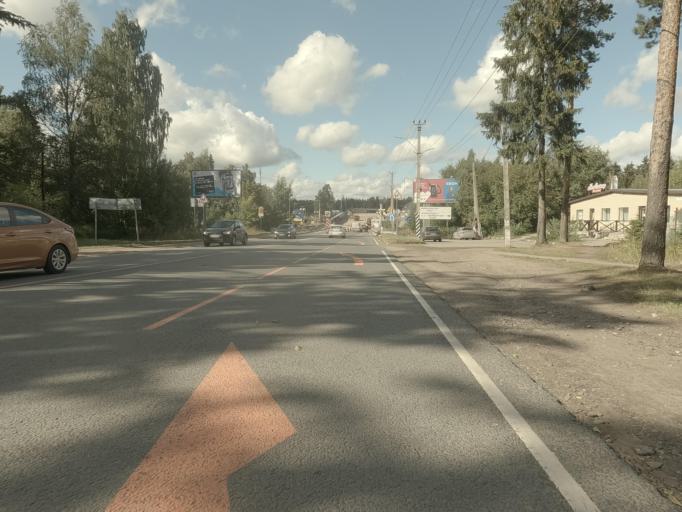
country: RU
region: Leningrad
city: Vsevolozhsk
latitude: 60.0121
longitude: 30.6664
